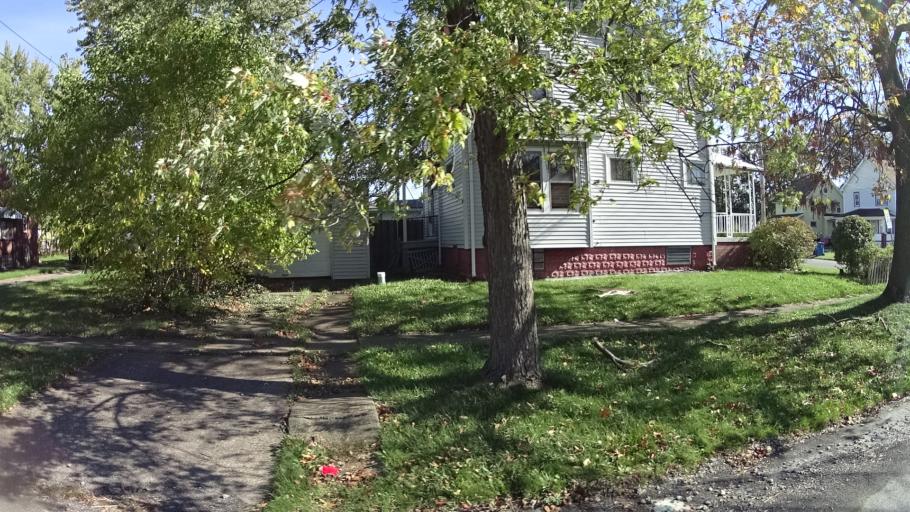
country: US
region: Ohio
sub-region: Lorain County
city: Lorain
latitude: 41.4519
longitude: -82.1749
